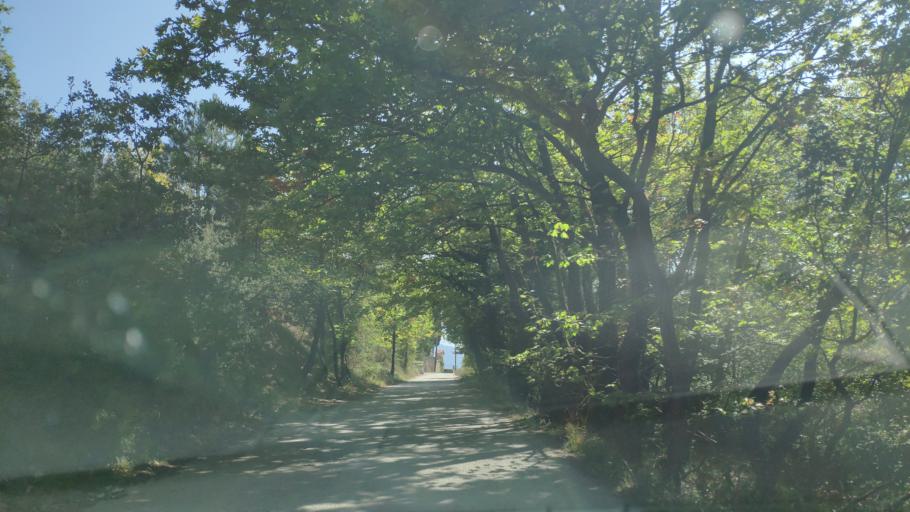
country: GR
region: West Greece
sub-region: Nomos Achaias
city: Kalavryta
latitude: 37.9219
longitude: 22.2948
